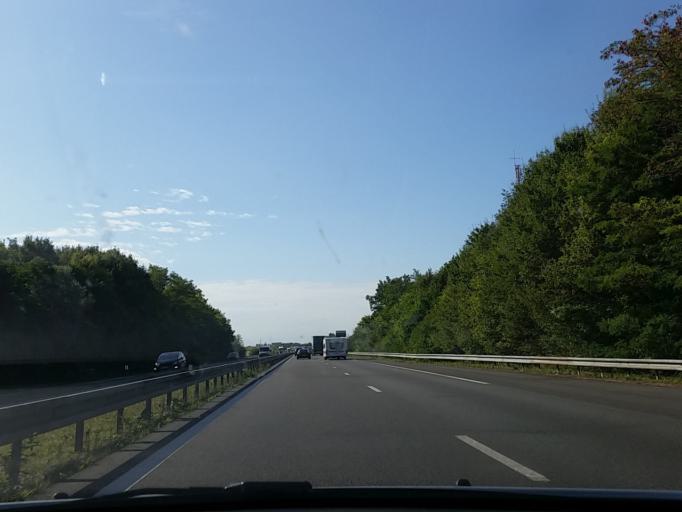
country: FR
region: Centre
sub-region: Departement du Cher
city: Mehun-sur-Yevre
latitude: 47.1451
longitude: 2.1855
